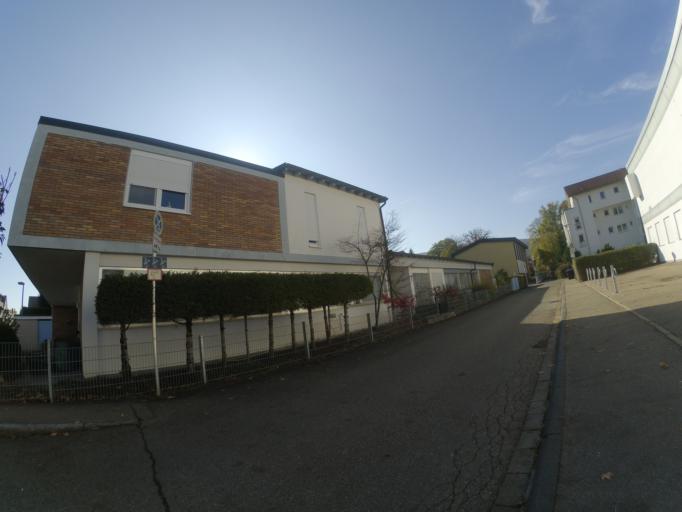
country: DE
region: Baden-Wuerttemberg
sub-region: Tuebingen Region
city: Blaubeuren
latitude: 48.4057
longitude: 9.7915
